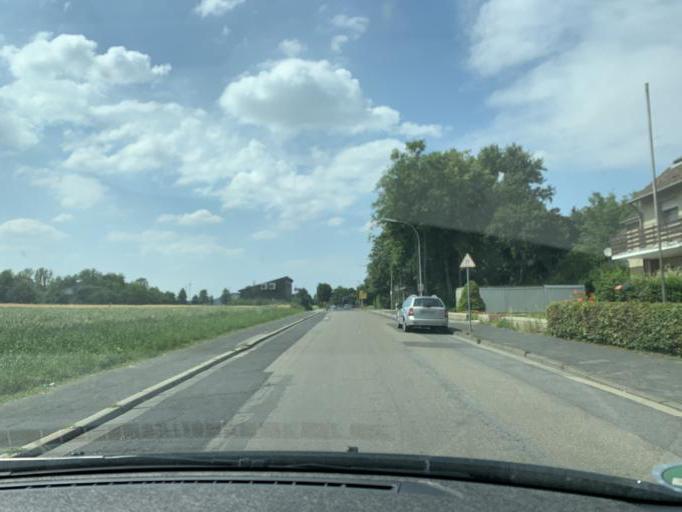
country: DE
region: North Rhine-Westphalia
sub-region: Regierungsbezirk Koln
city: Bedburg
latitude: 51.0402
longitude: 6.5883
